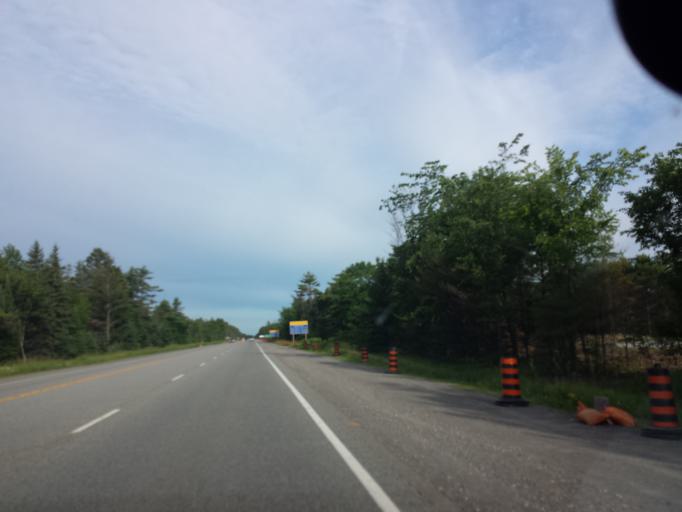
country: CA
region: Ontario
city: Arnprior
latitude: 45.4358
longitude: -76.4183
